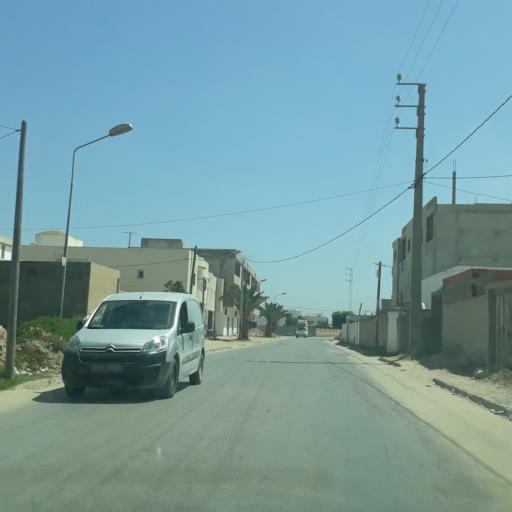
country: TN
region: Safaqis
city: Al Qarmadah
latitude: 34.8111
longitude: 10.7637
